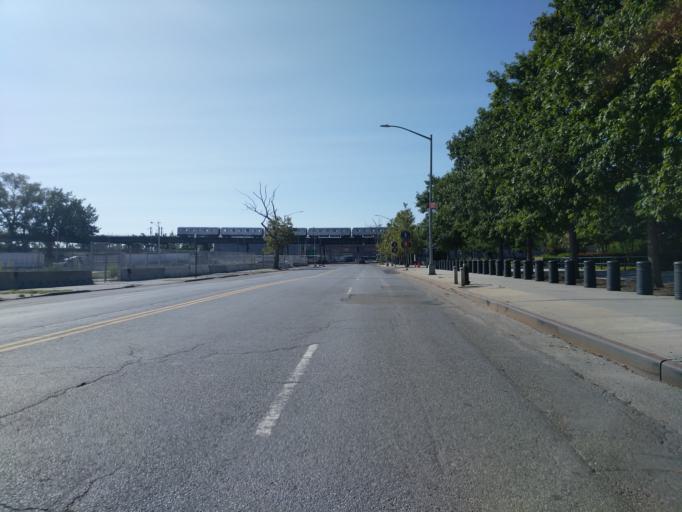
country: US
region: New York
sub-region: Queens County
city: Borough of Queens
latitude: 40.7569
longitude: -73.8441
